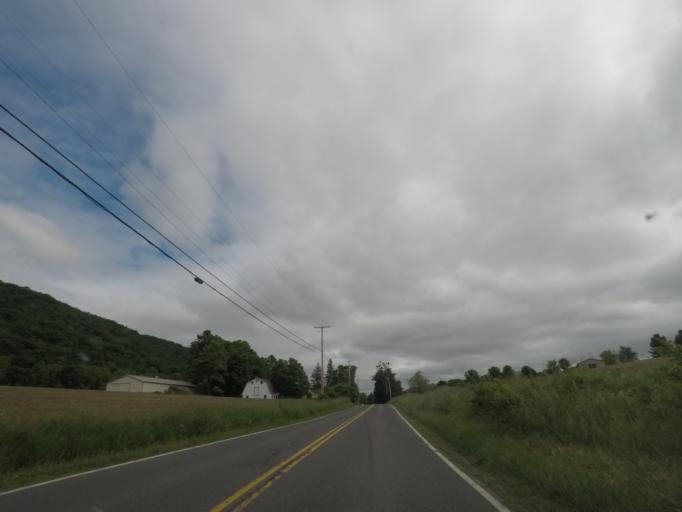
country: US
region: New York
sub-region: Dutchess County
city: Pine Plains
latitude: 41.9879
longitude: -73.5082
